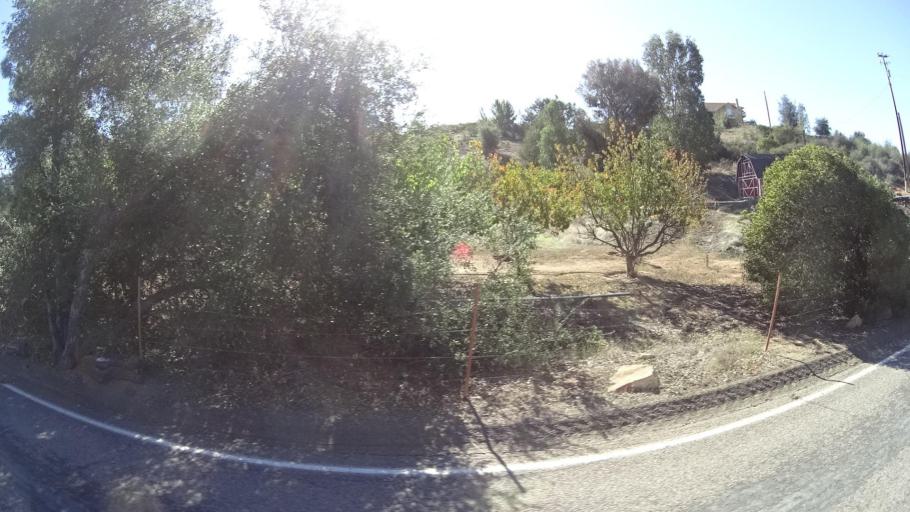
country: US
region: California
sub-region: San Diego County
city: Jamul
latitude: 32.7106
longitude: -116.7827
